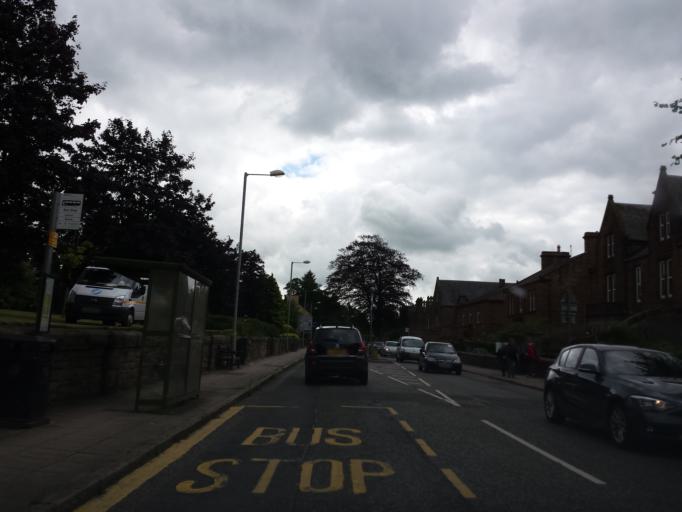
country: GB
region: Scotland
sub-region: Dumfries and Galloway
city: Dumfries
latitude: 55.0624
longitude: -3.6039
